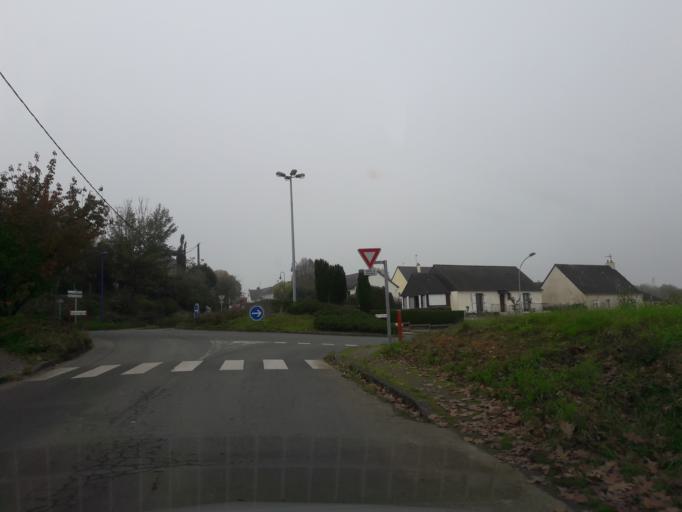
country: FR
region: Brittany
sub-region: Departement d'Ille-et-Vilaine
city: Janze
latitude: 47.9645
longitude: -1.4984
